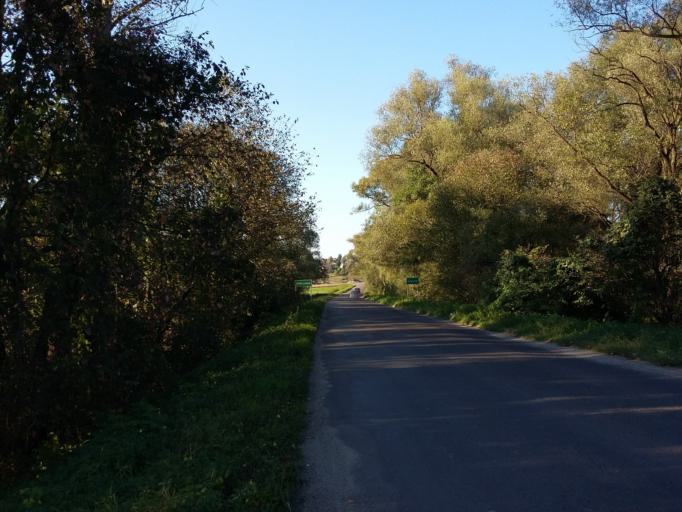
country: PL
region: Subcarpathian Voivodeship
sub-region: Powiat jasielski
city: Tarnowiec
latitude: 49.7467
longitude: 21.5901
